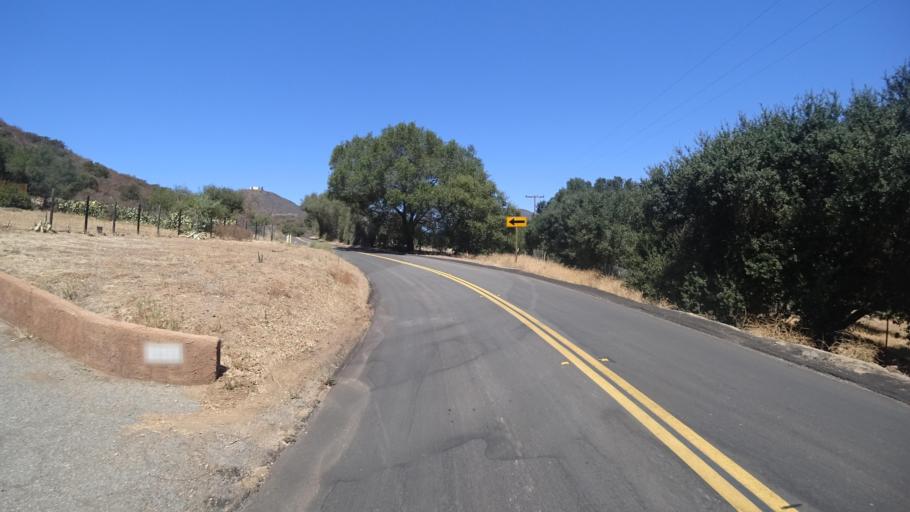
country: US
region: California
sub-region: San Diego County
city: Rainbow
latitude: 33.3544
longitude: -117.1359
